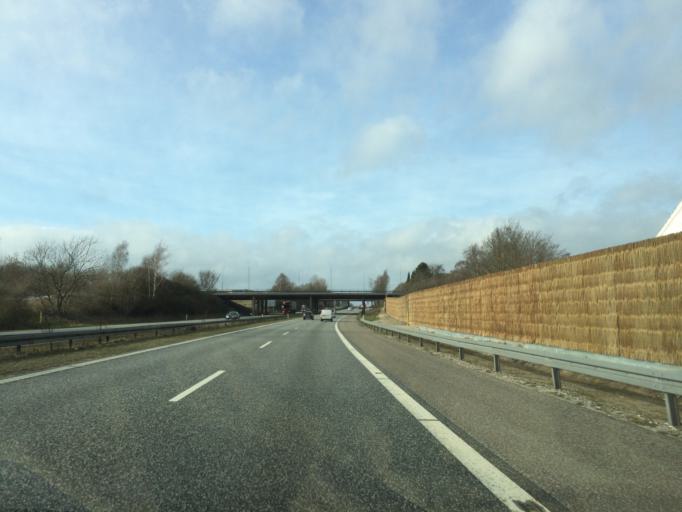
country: DK
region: Central Jutland
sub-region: Randers Kommune
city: Randers
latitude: 56.4604
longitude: 9.9876
